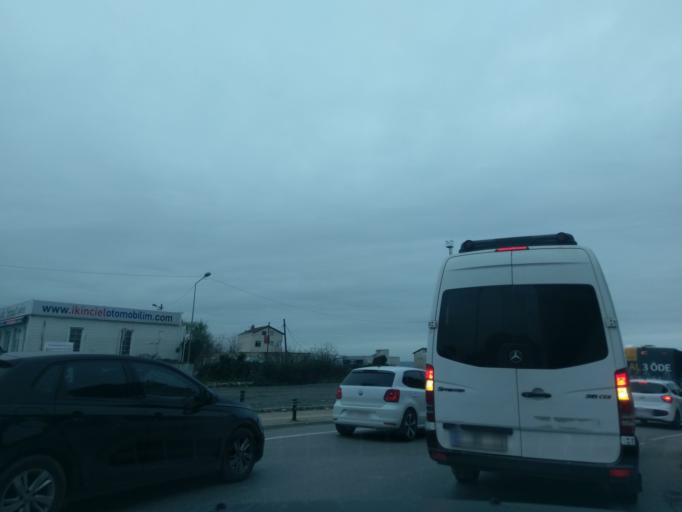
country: TR
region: Istanbul
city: Umraniye
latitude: 41.0948
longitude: 29.0970
